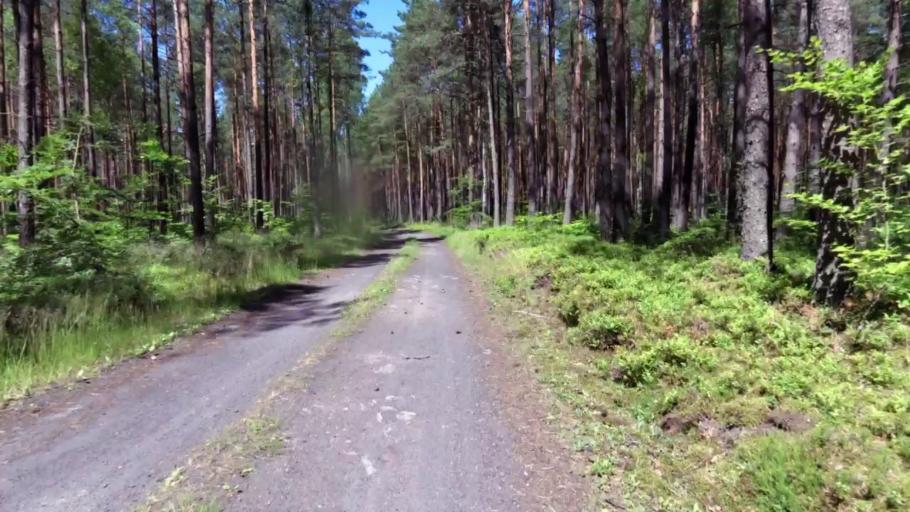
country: PL
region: West Pomeranian Voivodeship
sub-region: Powiat bialogardzki
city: Bialogard
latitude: 53.9482
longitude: 16.1144
